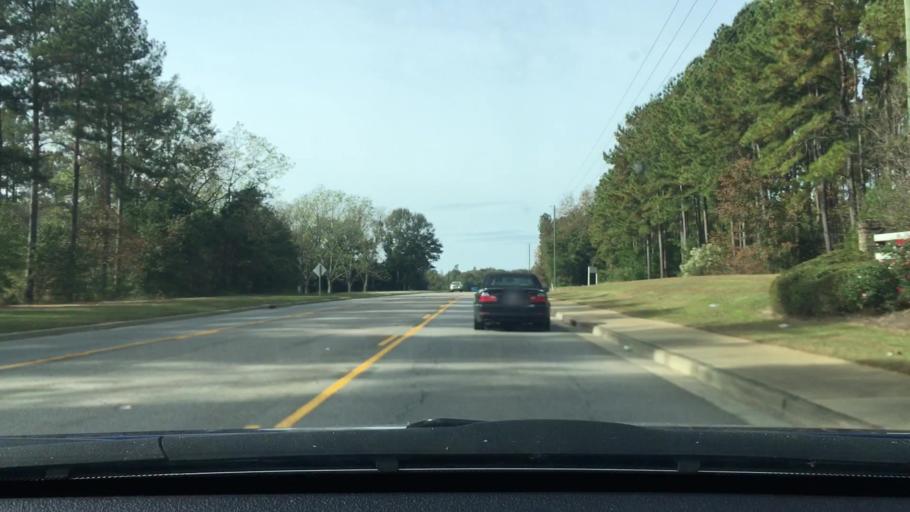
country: US
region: South Carolina
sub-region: Sumter County
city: South Sumter
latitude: 33.9204
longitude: -80.3952
